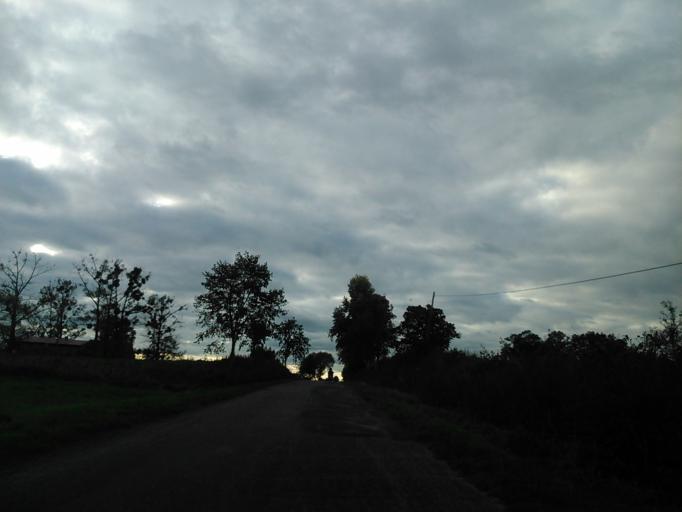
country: PL
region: Kujawsko-Pomorskie
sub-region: Powiat golubsko-dobrzynski
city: Kowalewo Pomorskie
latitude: 53.1189
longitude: 18.9076
